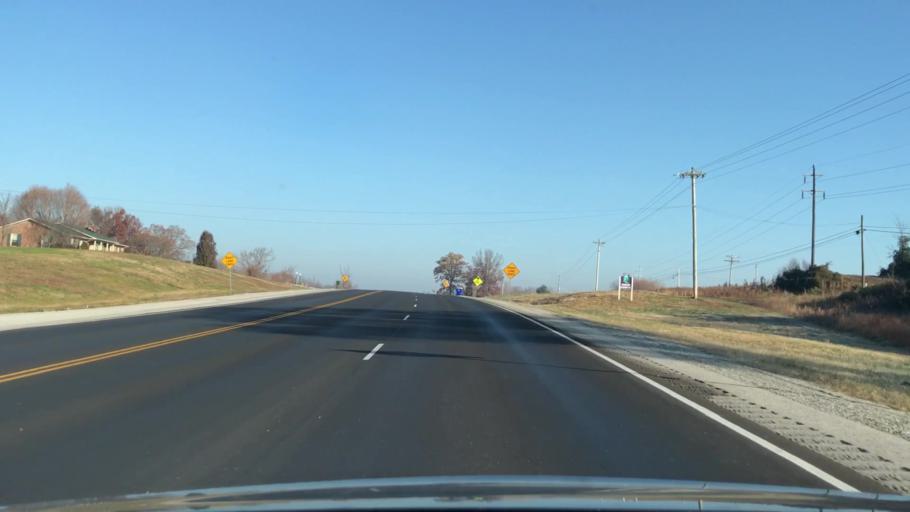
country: US
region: Kentucky
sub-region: Edmonson County
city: Brownsville
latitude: 37.1021
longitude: -86.2296
